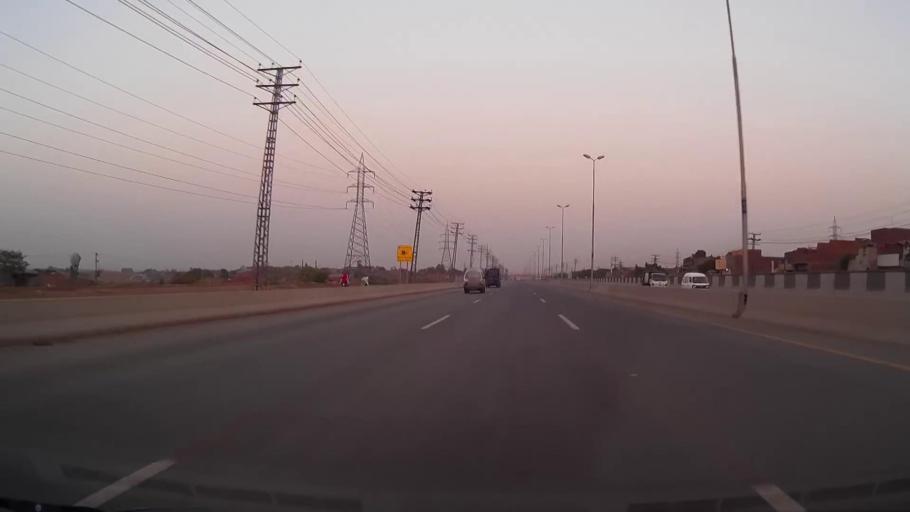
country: PK
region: Punjab
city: Lahore
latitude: 31.6094
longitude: 74.3306
